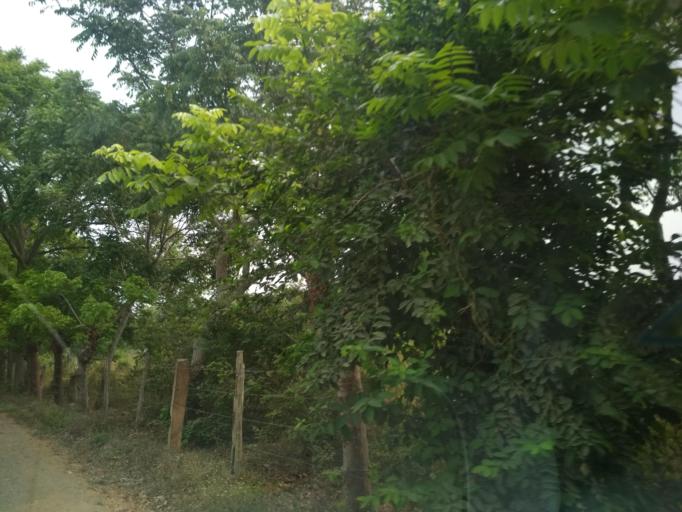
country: MX
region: Veracruz
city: Paso del Toro
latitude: 19.0205
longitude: -96.1502
